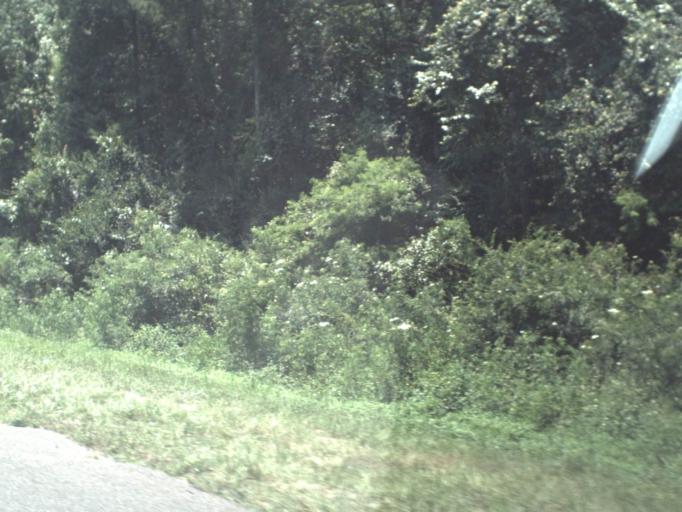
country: US
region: Florida
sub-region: Putnam County
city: Palatka
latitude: 29.4830
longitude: -81.7415
